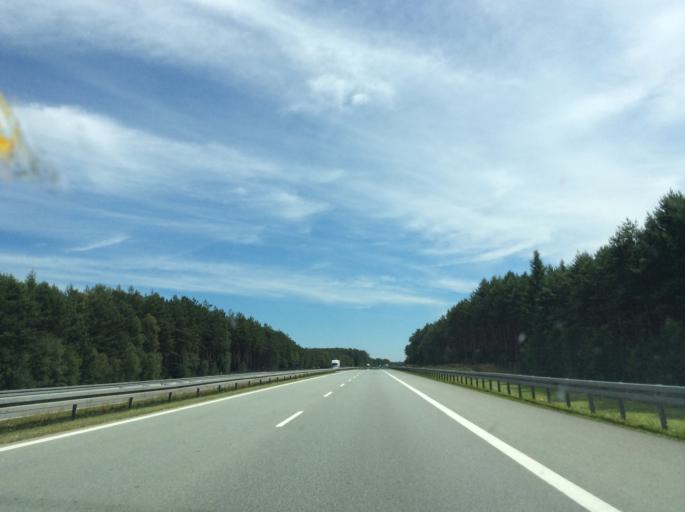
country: PL
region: Greater Poland Voivodeship
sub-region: Powiat nowotomyski
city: Nowy Tomysl
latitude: 52.3662
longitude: 16.1545
